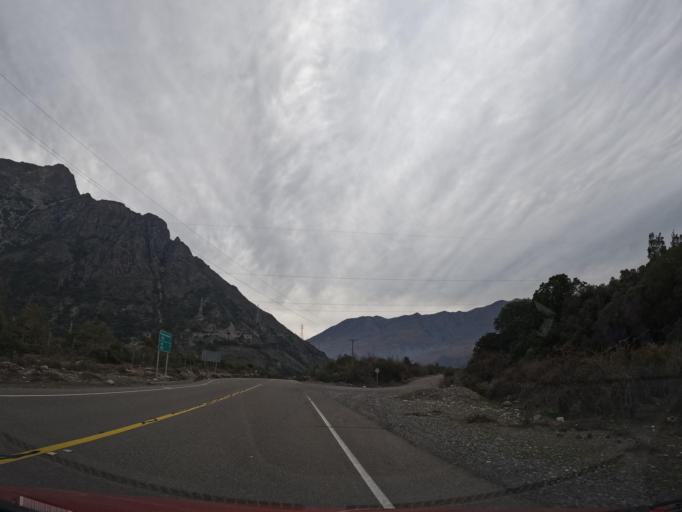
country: CL
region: Maule
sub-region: Provincia de Linares
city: Colbun
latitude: -35.7104
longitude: -71.0705
